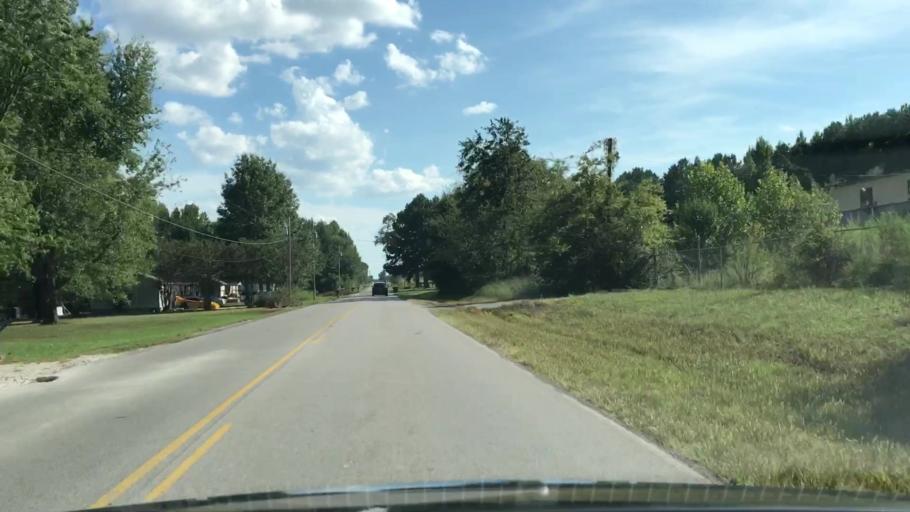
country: US
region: Alabama
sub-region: Madison County
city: Harvest
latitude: 34.8815
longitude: -86.7488
